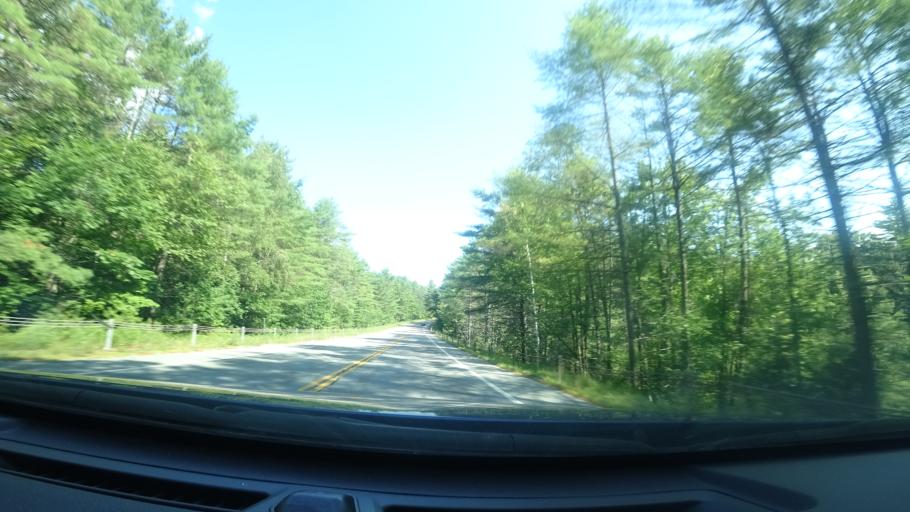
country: US
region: New York
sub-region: Warren County
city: Warrensburg
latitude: 43.6050
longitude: -73.8032
